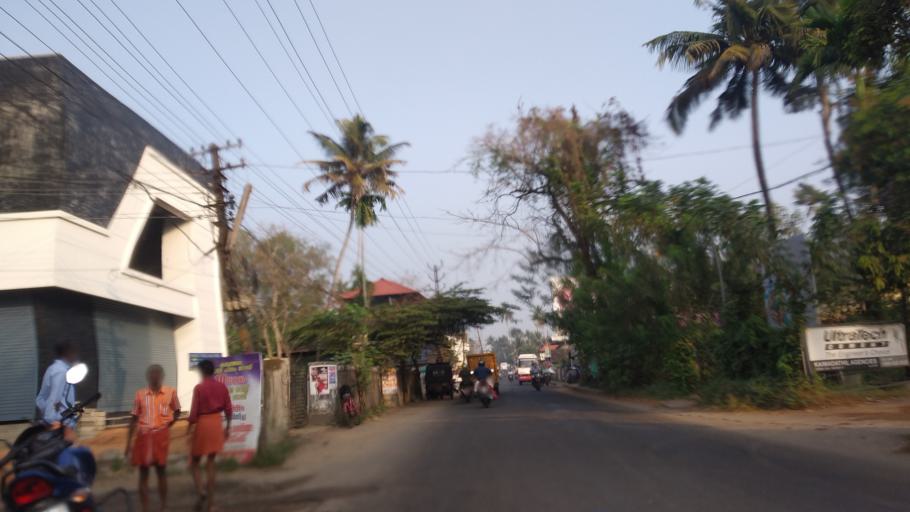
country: IN
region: Kerala
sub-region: Thrissur District
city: Kodungallur
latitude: 10.1439
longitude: 76.1919
